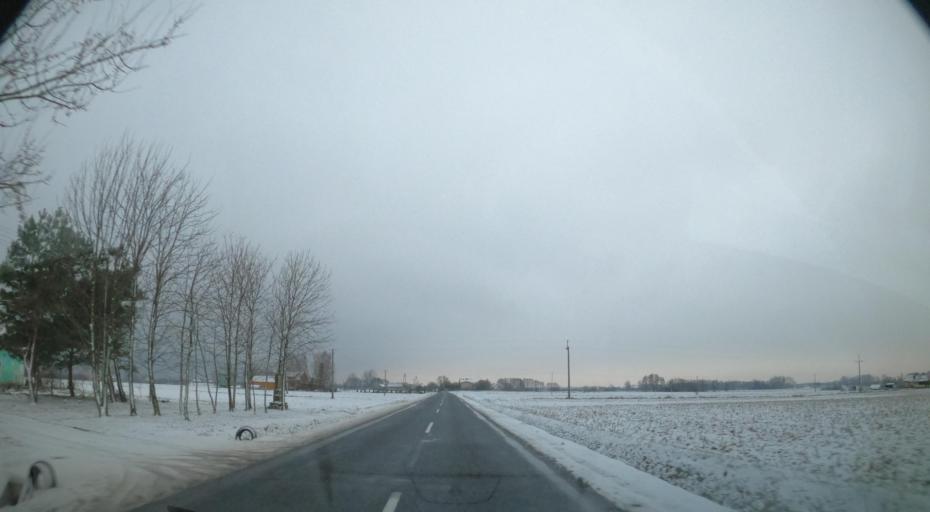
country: PL
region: Masovian Voivodeship
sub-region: Powiat plocki
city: Nowy Duninow
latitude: 52.6279
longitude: 19.4295
